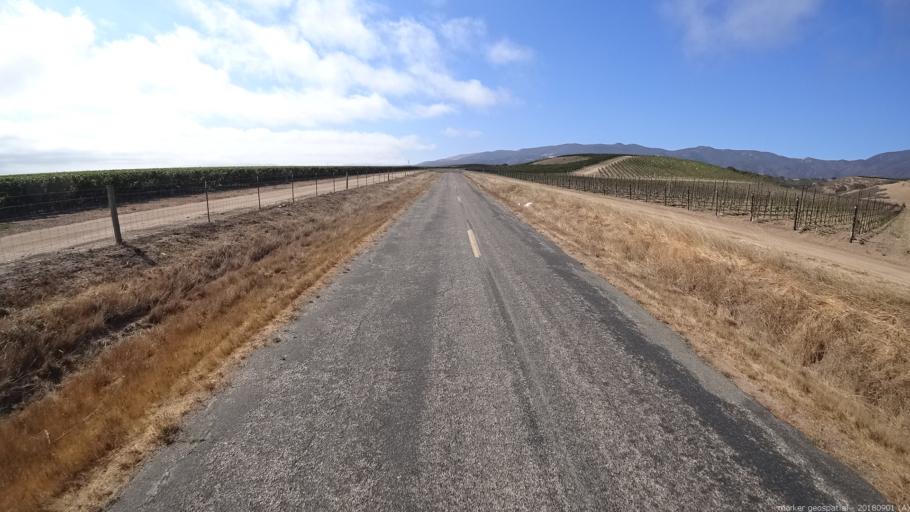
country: US
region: California
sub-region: Monterey County
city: Soledad
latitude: 36.3543
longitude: -121.3356
